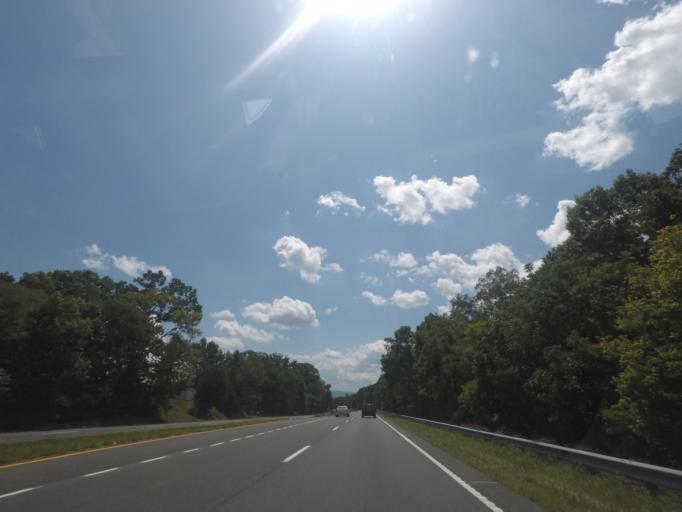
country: US
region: Virginia
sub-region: City of Winchester
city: Winchester
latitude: 39.1031
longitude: -78.1137
